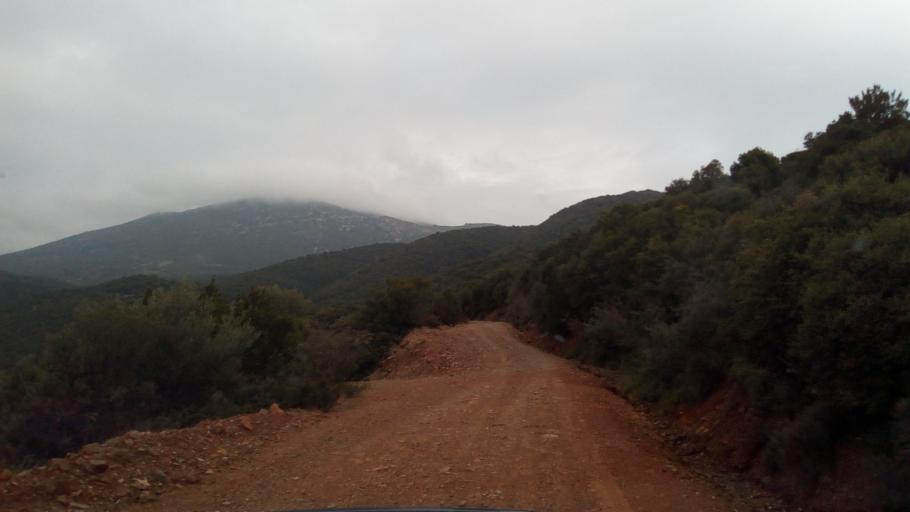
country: GR
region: West Greece
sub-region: Nomos Achaias
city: Temeni
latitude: 38.3641
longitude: 22.1589
